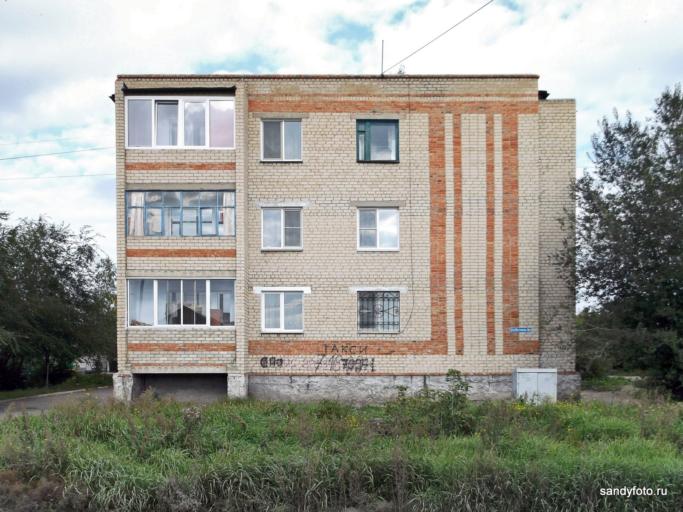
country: RU
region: Chelyabinsk
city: Troitsk
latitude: 54.1077
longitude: 61.5726
